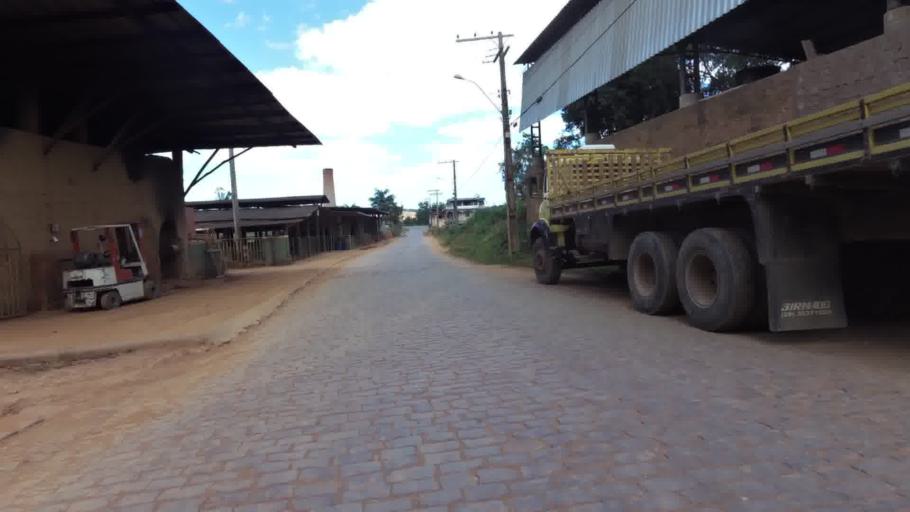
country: BR
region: Espirito Santo
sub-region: Rio Novo Do Sul
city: Rio Novo do Sul
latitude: -20.8706
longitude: -40.9459
